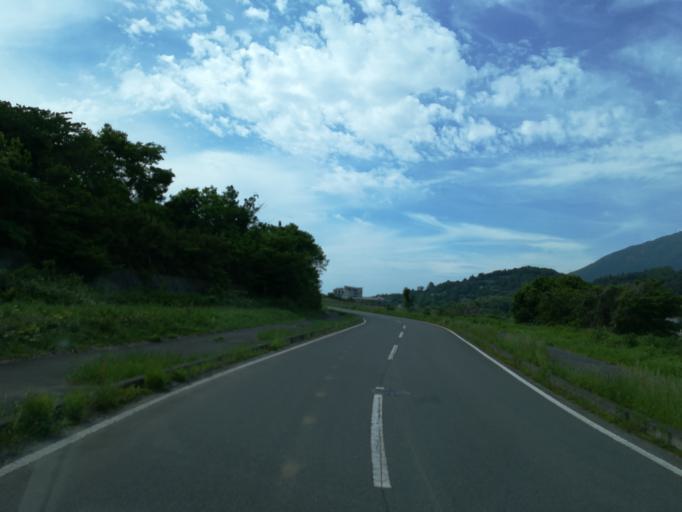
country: JP
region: Ibaraki
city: Tsukuba
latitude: 36.1764
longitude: 140.1014
